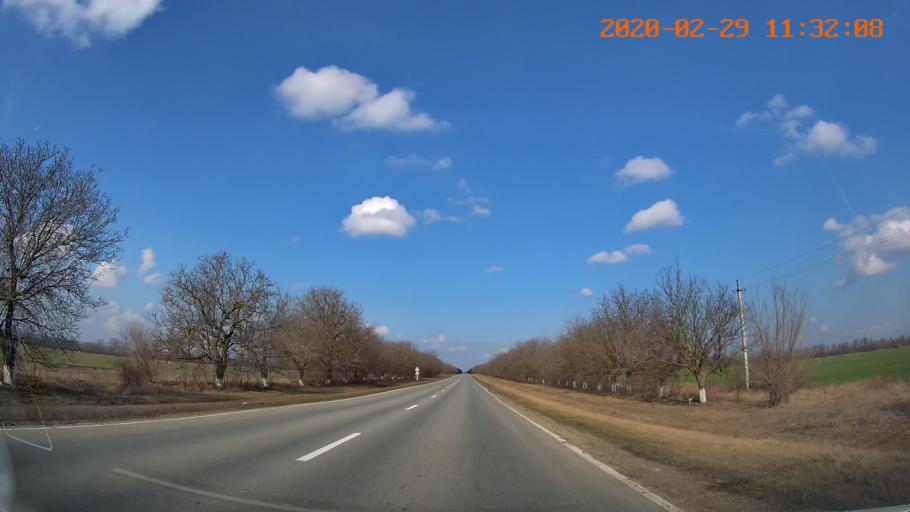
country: MD
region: Rezina
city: Saharna
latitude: 47.5337
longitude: 29.0976
